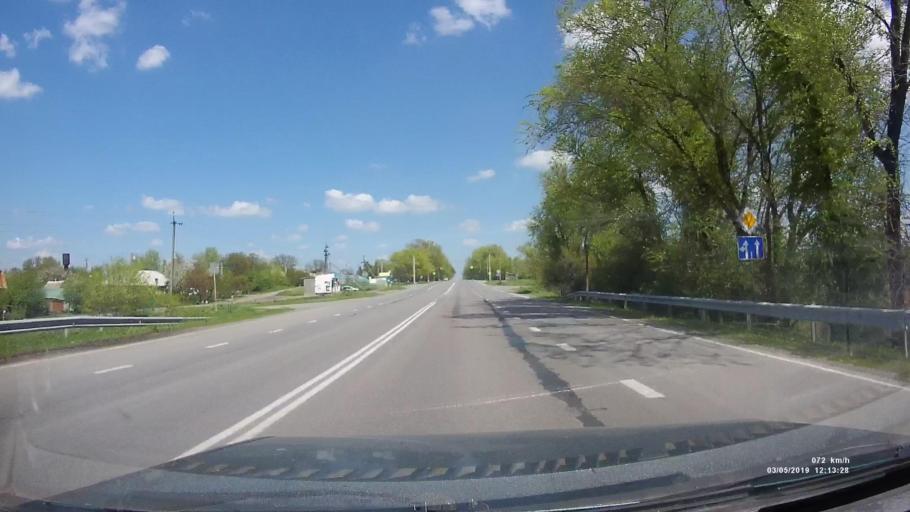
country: RU
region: Rostov
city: Melikhovskaya
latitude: 47.3330
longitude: 40.5552
